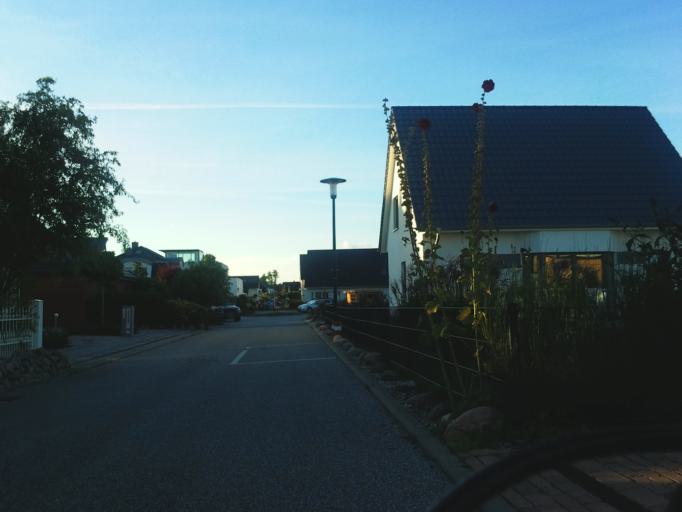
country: DE
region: Mecklenburg-Vorpommern
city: Rostock
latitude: 54.1132
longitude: 12.1024
